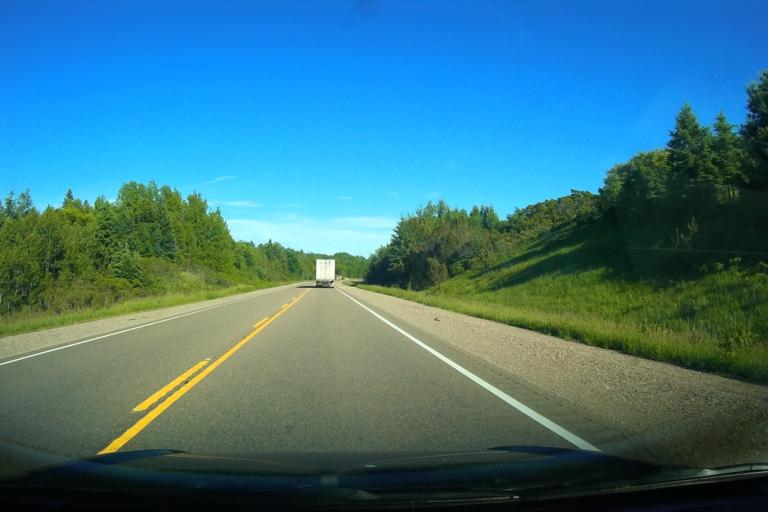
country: CA
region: Ontario
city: Renfrew
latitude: 45.5544
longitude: -76.7383
